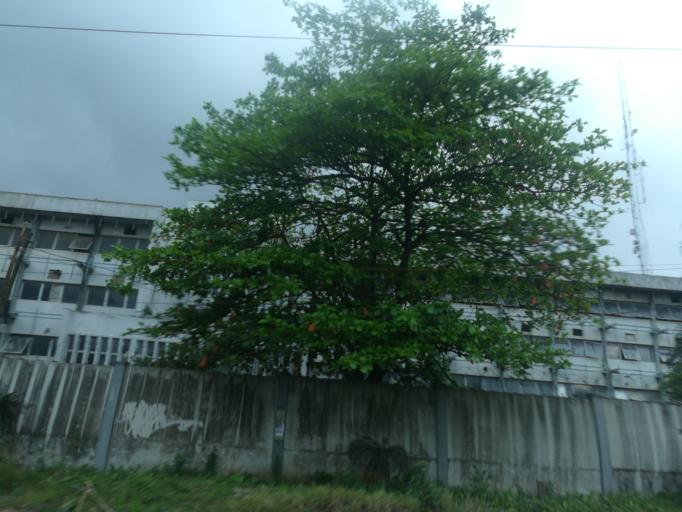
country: NG
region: Lagos
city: Agege
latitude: 6.6094
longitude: 3.3362
